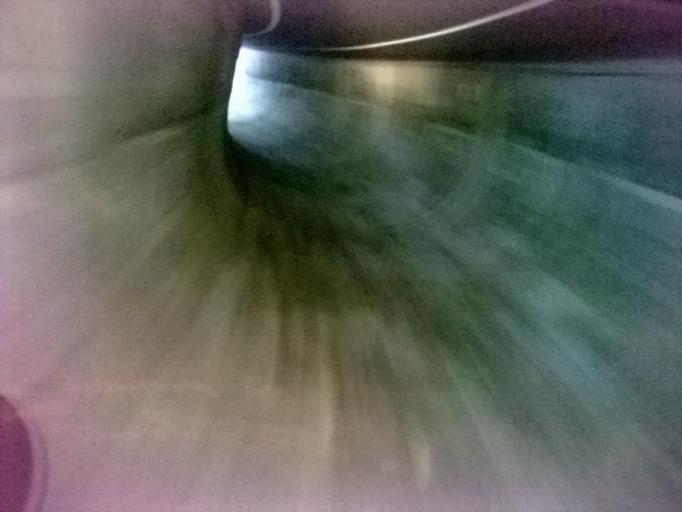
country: ME
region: Opstina Pluzine
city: Pluzine
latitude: 43.2364
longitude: 18.8439
